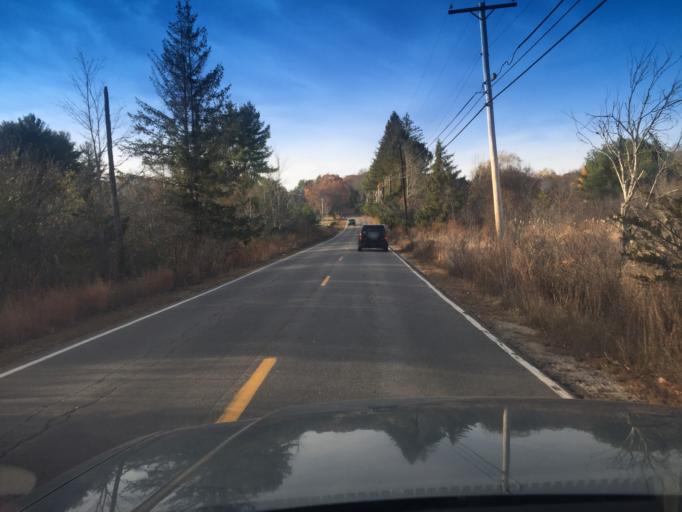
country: US
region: Maine
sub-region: York County
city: Eliot
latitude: 43.1829
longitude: -70.7393
